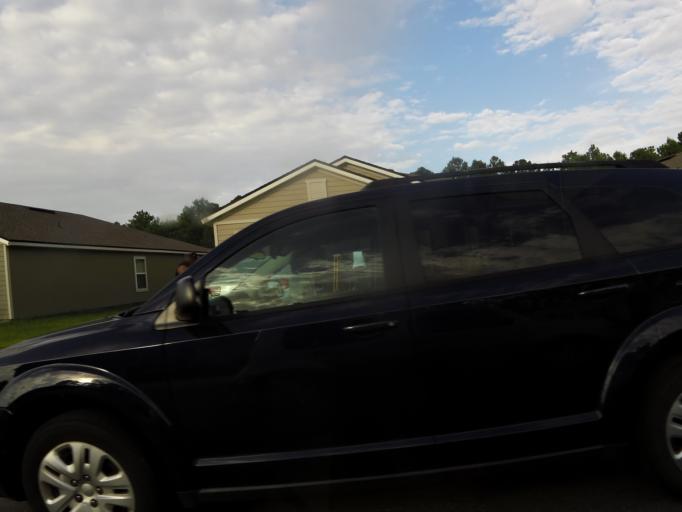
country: US
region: Florida
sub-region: Duval County
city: Jacksonville
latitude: 30.3578
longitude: -81.7700
